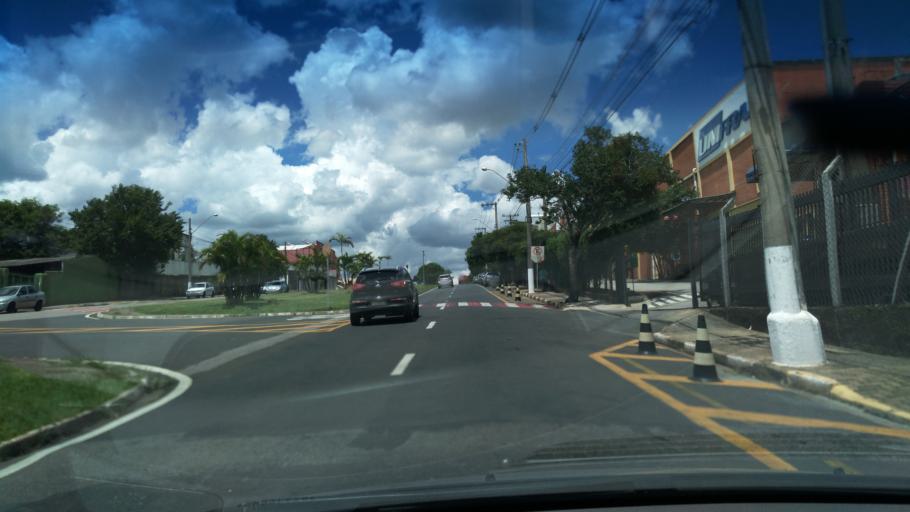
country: BR
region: Sao Paulo
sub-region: Vinhedo
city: Vinhedo
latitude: -23.0114
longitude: -46.9872
